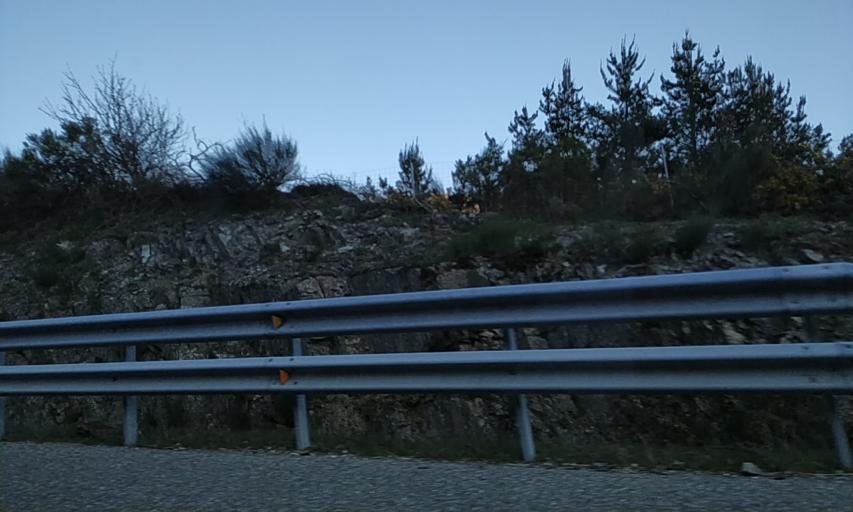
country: ES
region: Galicia
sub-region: Provincia de Lugo
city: Baralla
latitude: 42.9147
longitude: -7.2274
